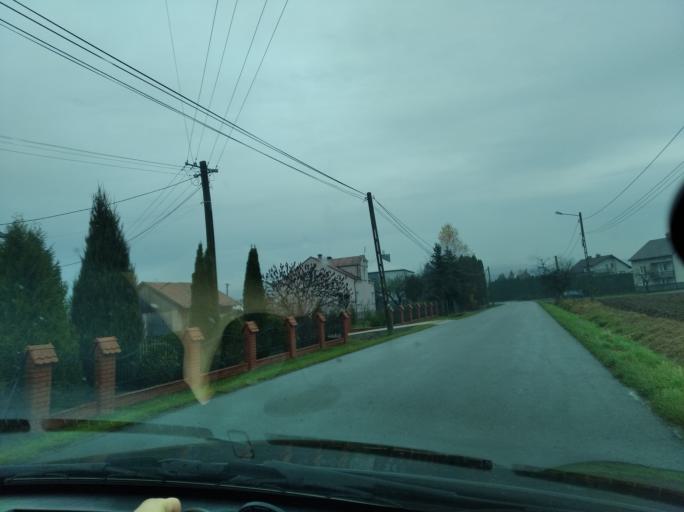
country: PL
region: Subcarpathian Voivodeship
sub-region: Powiat strzyzowski
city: Babica
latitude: 49.9258
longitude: 21.8577
